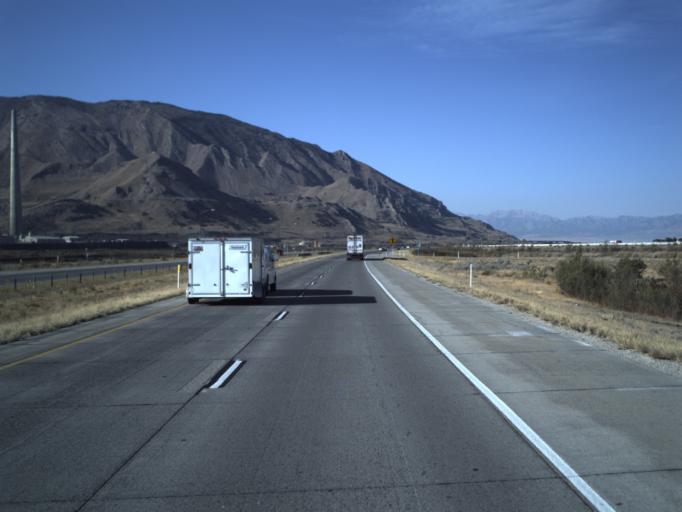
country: US
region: Utah
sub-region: Salt Lake County
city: Magna
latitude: 40.7437
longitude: -112.1852
